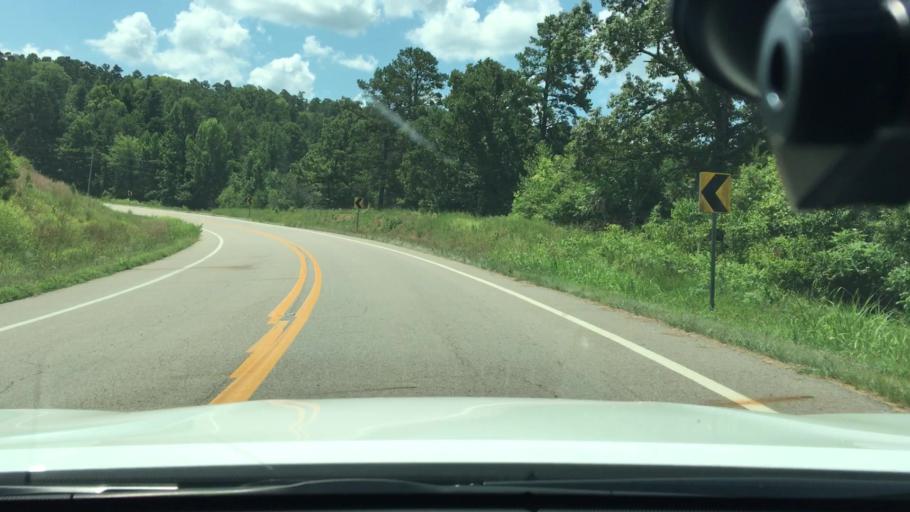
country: US
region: Arkansas
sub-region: Logan County
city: Paris
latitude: 35.2579
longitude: -93.6833
